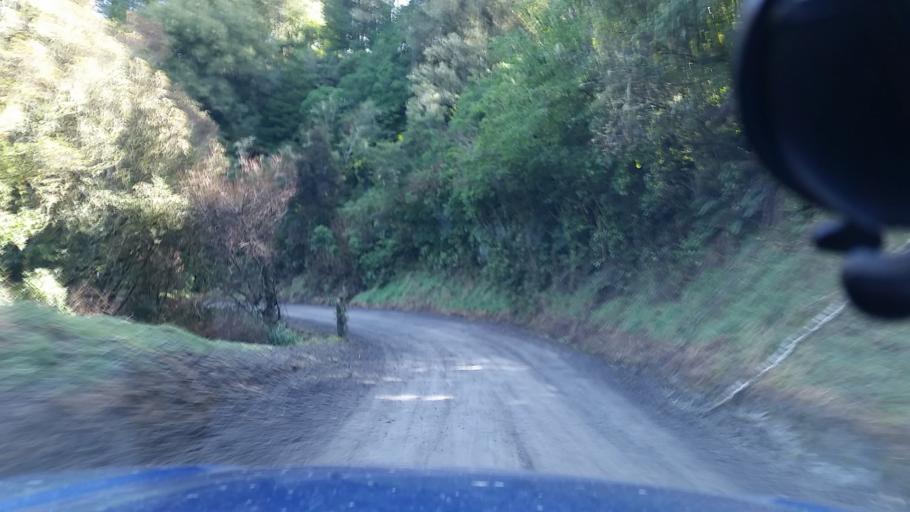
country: NZ
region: Taranaki
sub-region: New Plymouth District
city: Waitara
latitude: -39.0618
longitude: 174.7878
